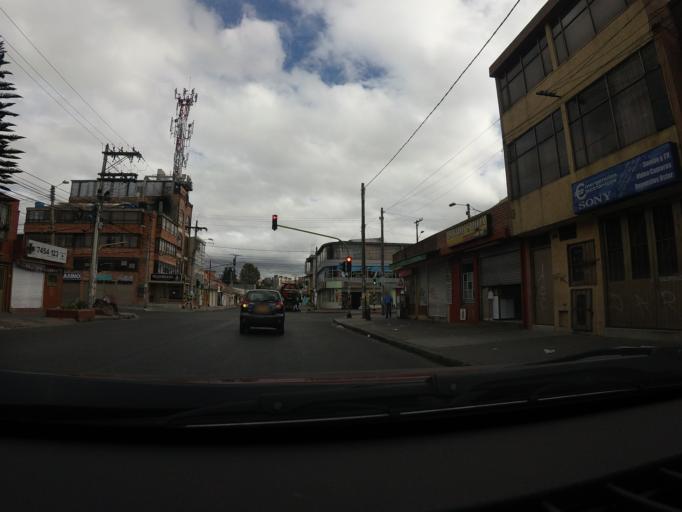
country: CO
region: Bogota D.C.
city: Bogota
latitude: 4.6412
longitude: -74.1402
